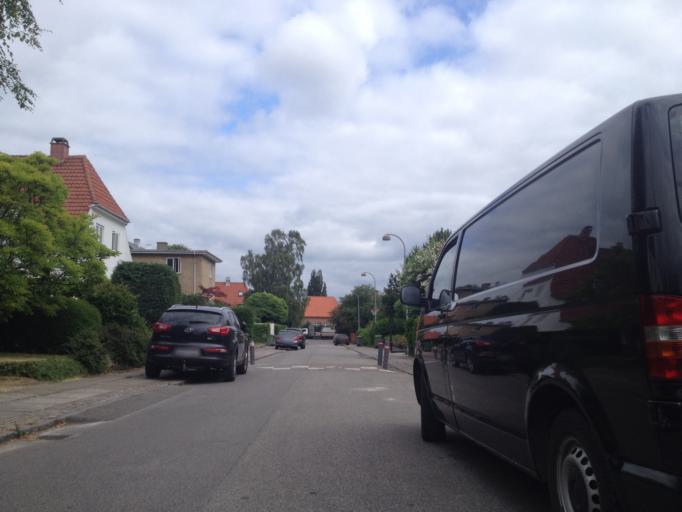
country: DK
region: Capital Region
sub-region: Gentofte Kommune
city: Charlottenlund
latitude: 55.7409
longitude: 12.5722
